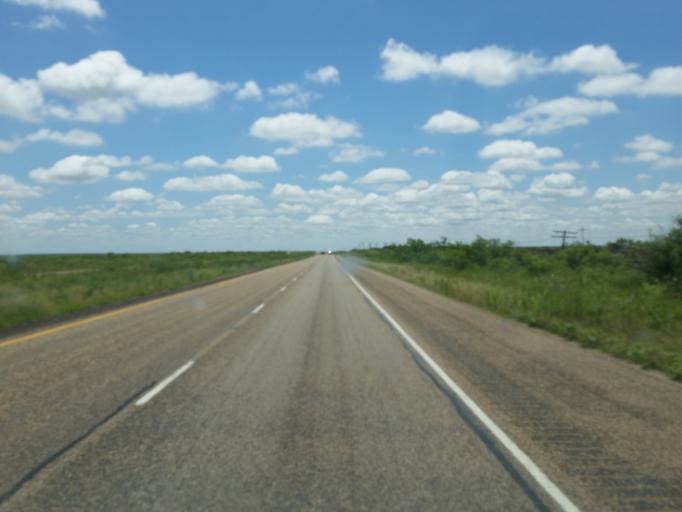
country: US
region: Texas
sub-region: Garza County
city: Post
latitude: 33.1289
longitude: -101.2969
